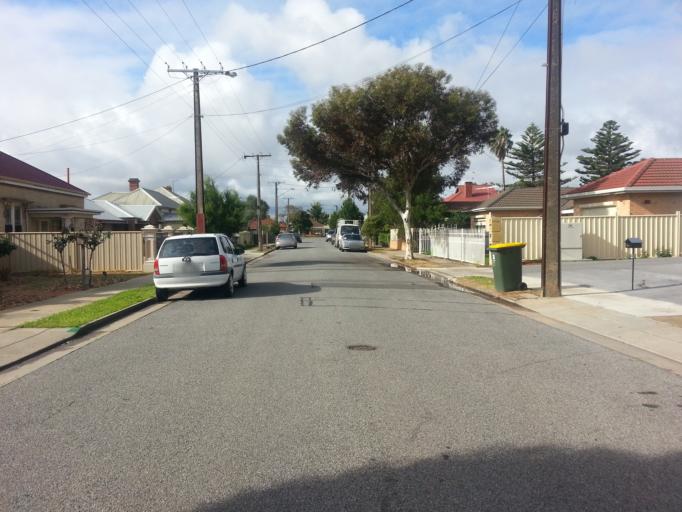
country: AU
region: South Australia
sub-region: Port Adelaide Enfield
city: Alberton
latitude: -34.8488
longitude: 138.5201
